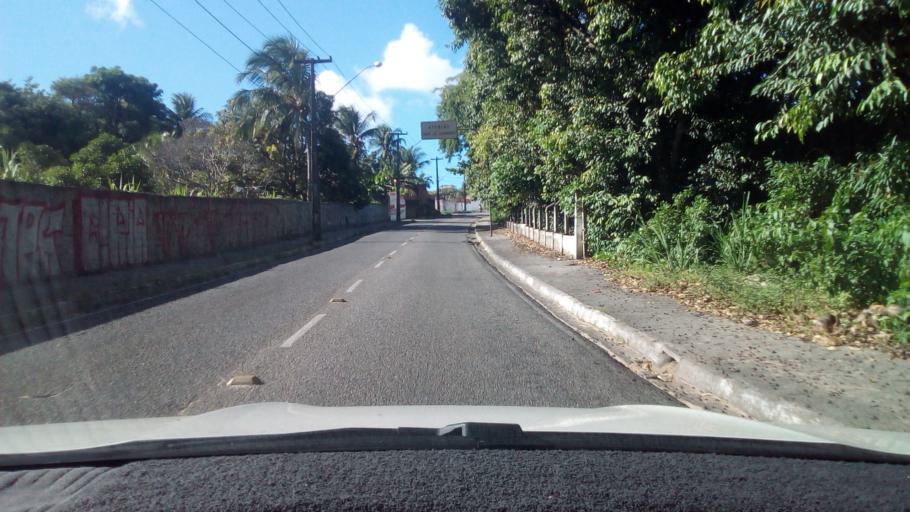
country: BR
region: Paraiba
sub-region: Joao Pessoa
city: Joao Pessoa
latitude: -7.1398
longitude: -34.8761
